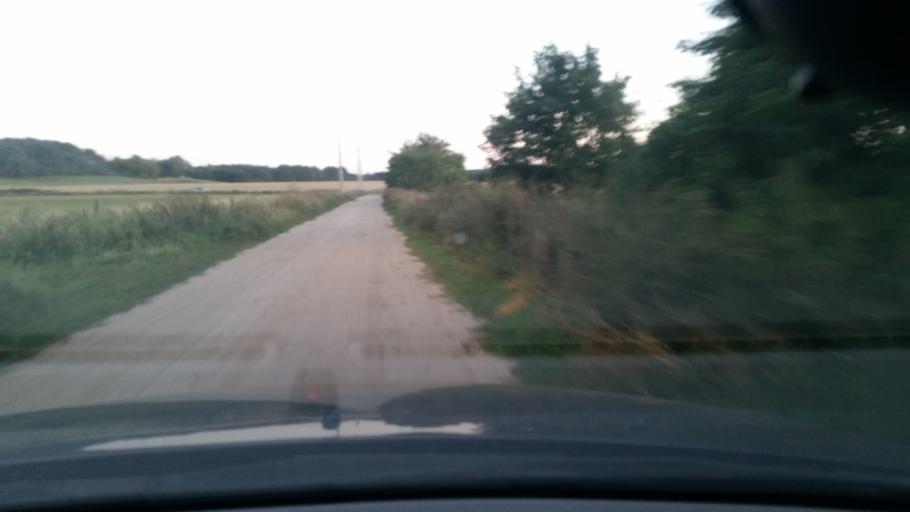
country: PL
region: Pomeranian Voivodeship
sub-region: Powiat wejherowski
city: Choczewo
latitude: 54.7776
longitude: 17.7920
